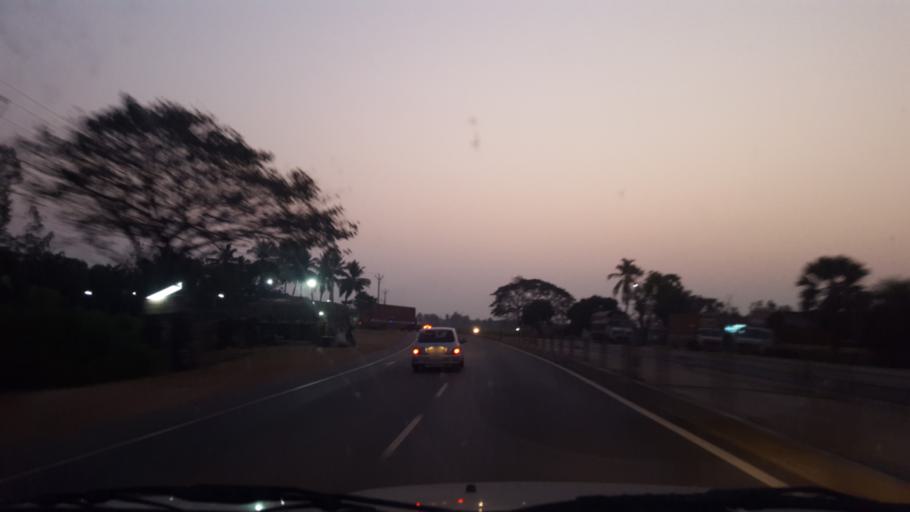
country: IN
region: Andhra Pradesh
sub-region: East Godavari
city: Peddapuram
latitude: 17.1475
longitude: 81.9817
